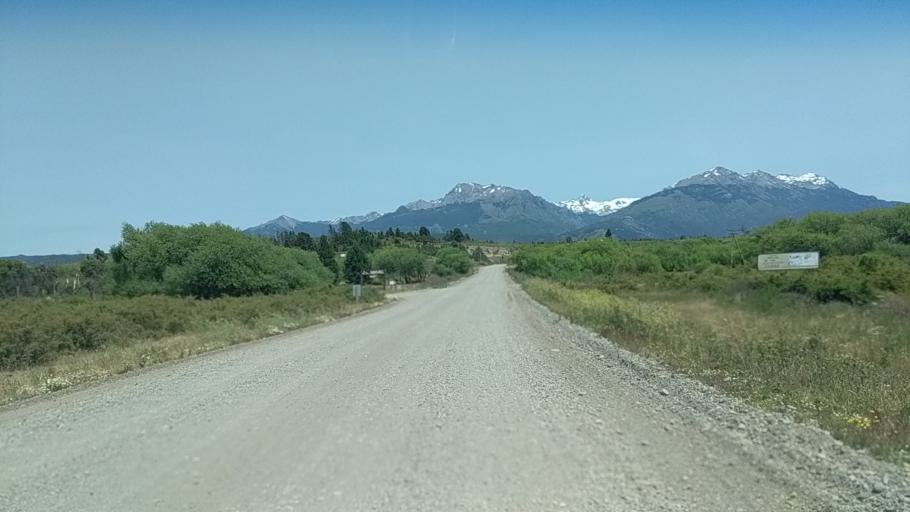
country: AR
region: Chubut
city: Trevelin
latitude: -43.1722
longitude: -71.5034
